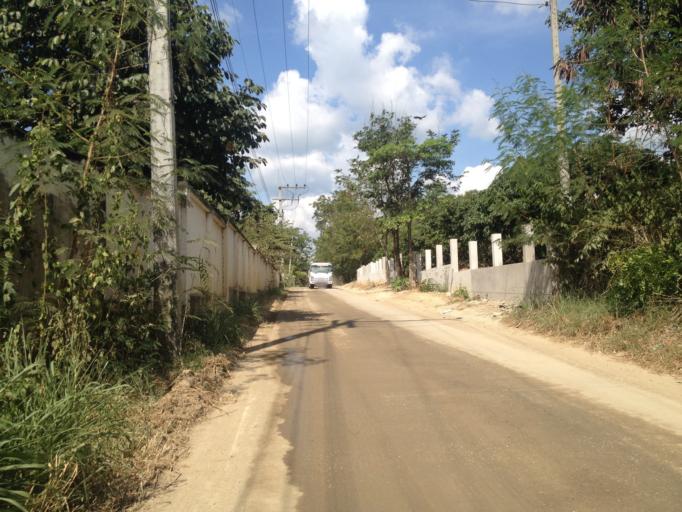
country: TH
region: Chiang Mai
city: Hang Dong
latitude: 18.6936
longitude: 98.8730
